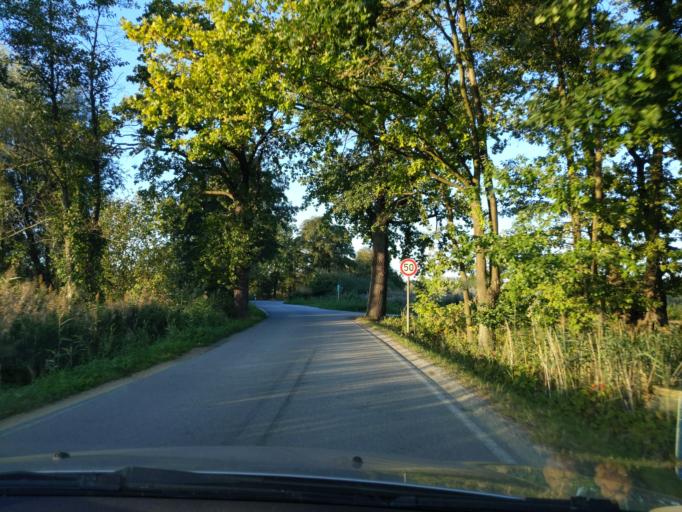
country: DE
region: Saxony
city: Guttau
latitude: 51.2666
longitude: 14.5671
